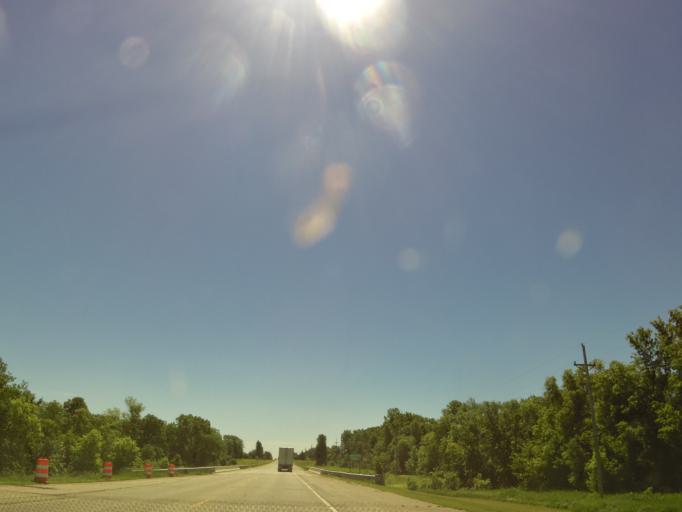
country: US
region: Minnesota
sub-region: Mahnomen County
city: Mahnomen
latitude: 47.3071
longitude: -95.9568
